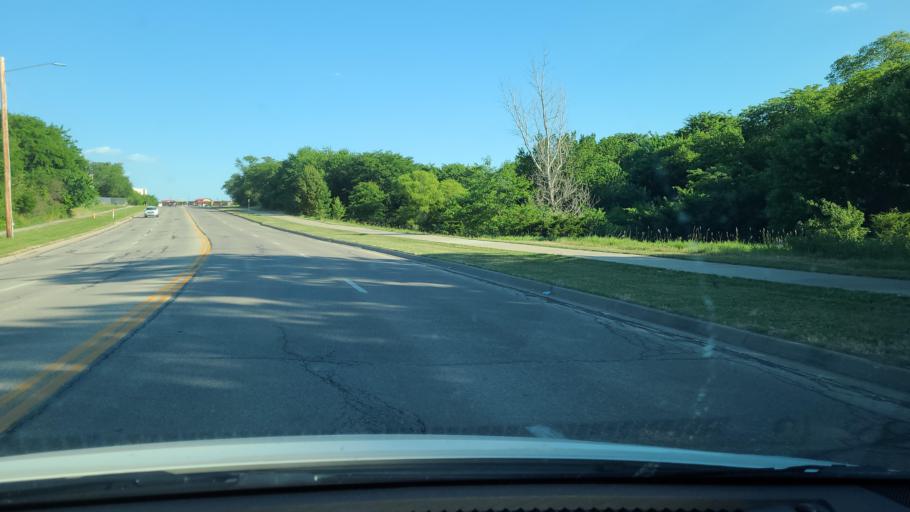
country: US
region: Kansas
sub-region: Douglas County
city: Lawrence
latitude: 38.9769
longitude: -95.3094
